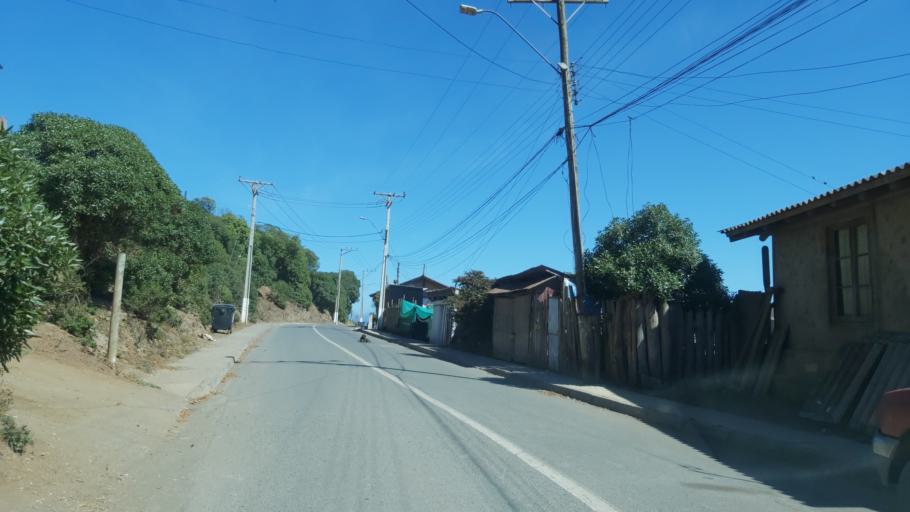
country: CL
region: Maule
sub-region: Provincia de Talca
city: Constitucion
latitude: -34.7547
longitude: -72.0842
